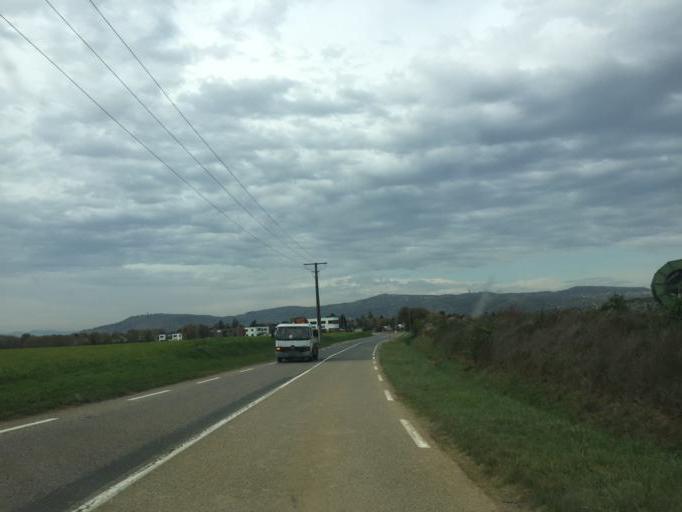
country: FR
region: Rhone-Alpes
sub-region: Departement du Rhone
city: Cailloux-sur-Fontaines
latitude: 45.8582
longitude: 4.8844
